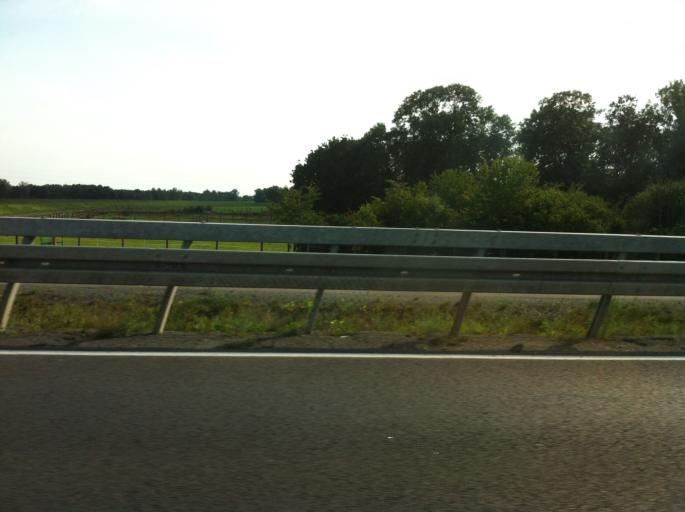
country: DE
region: Saxony
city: Markkleeberg
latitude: 51.2993
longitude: 12.3407
